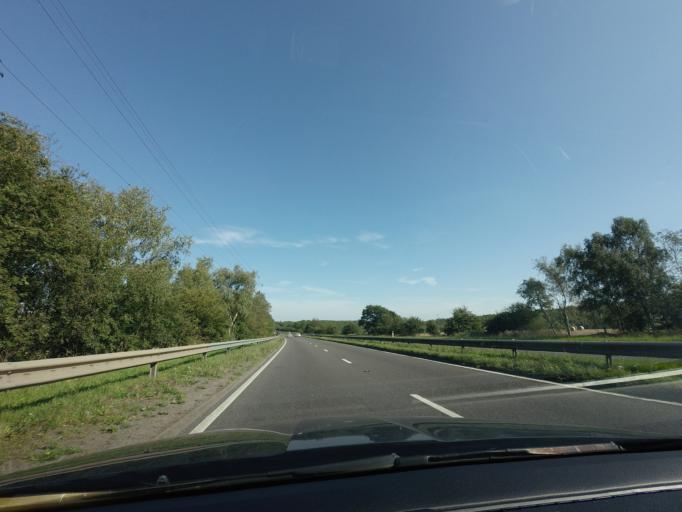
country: GB
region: England
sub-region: Derbyshire
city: Pilsley
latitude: 53.2020
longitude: -1.3636
